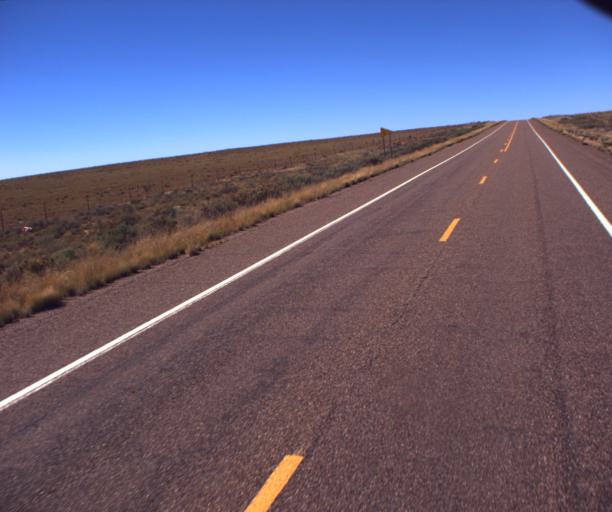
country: US
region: Arizona
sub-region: Navajo County
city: Holbrook
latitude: 34.8552
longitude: -109.9871
